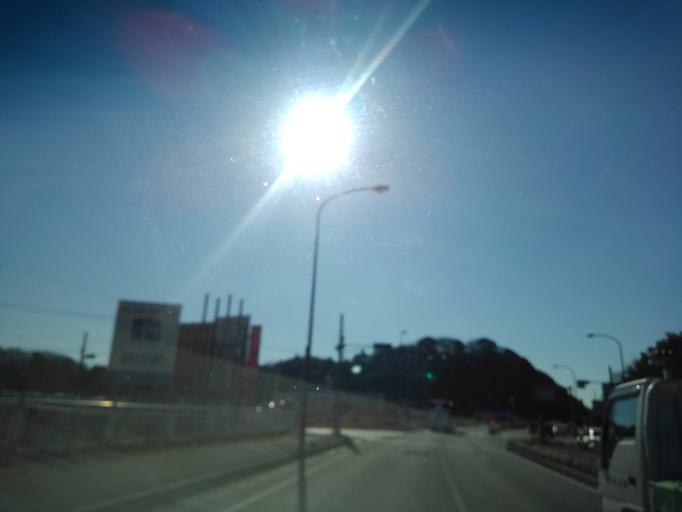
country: JP
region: Chiba
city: Kisarazu
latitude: 35.3477
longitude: 139.9211
